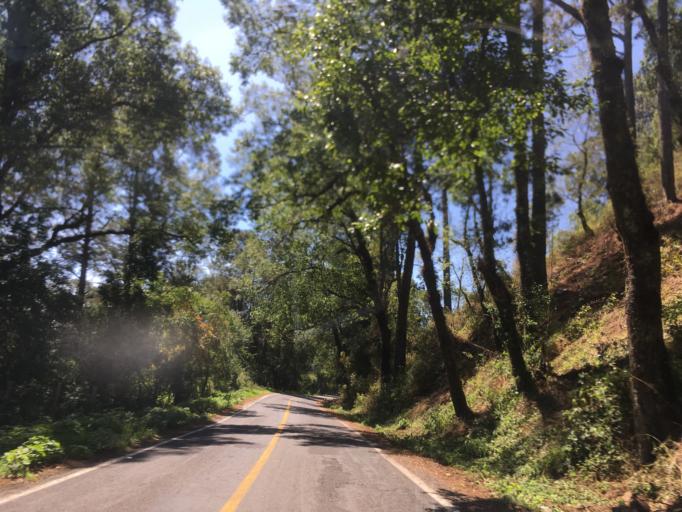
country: MX
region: Michoacan
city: Tzitzio
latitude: 19.6542
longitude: -100.7968
